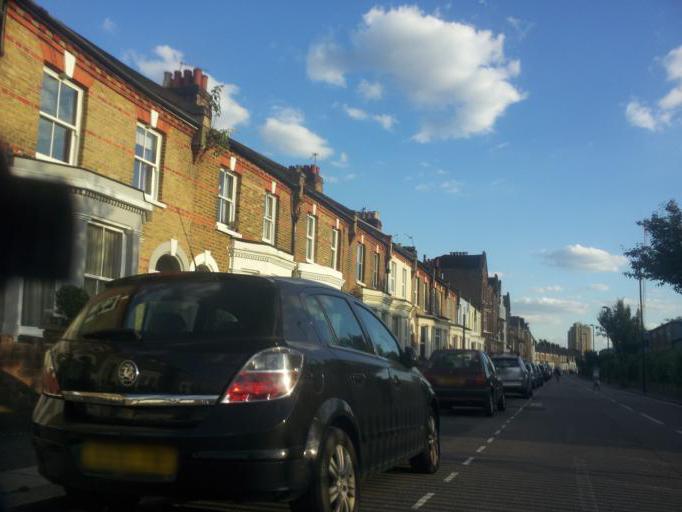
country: GB
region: England
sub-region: Greater London
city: Brixton
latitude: 51.4601
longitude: -0.1019
